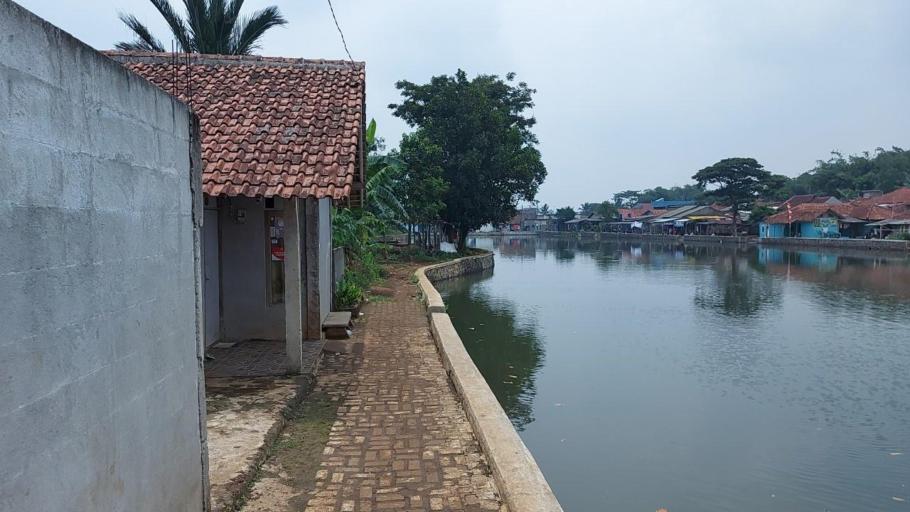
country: ID
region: West Java
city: Cibinong
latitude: -6.5297
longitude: 106.8155
